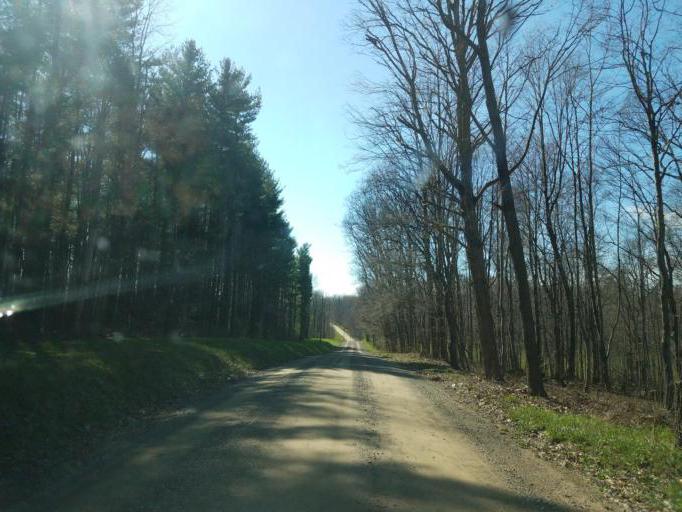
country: US
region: Ohio
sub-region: Knox County
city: Oak Hill
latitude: 40.4349
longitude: -82.2291
